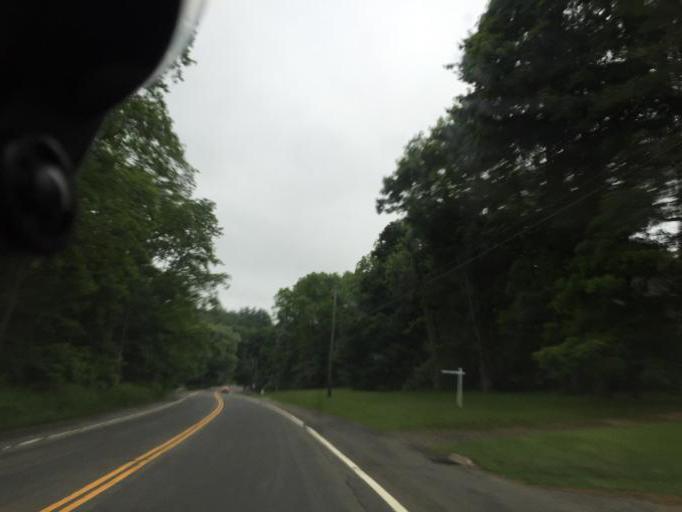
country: US
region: Connecticut
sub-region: Litchfield County
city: Canaan
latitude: 41.9401
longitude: -73.3031
